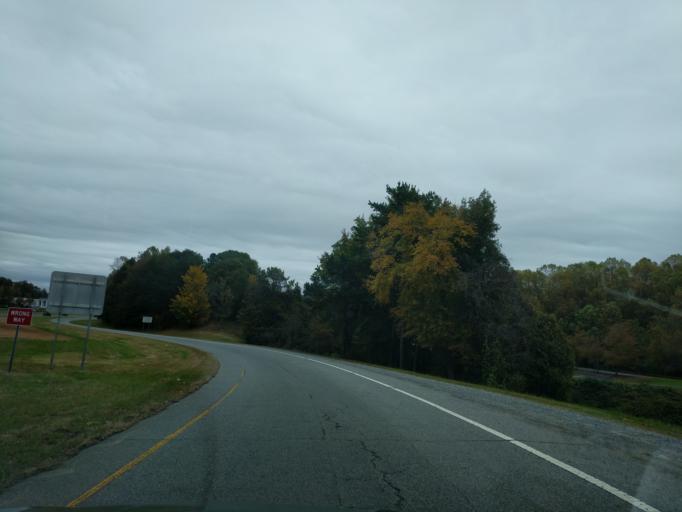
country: US
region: North Carolina
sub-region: Davidson County
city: Lexington
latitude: 35.7794
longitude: -80.2590
